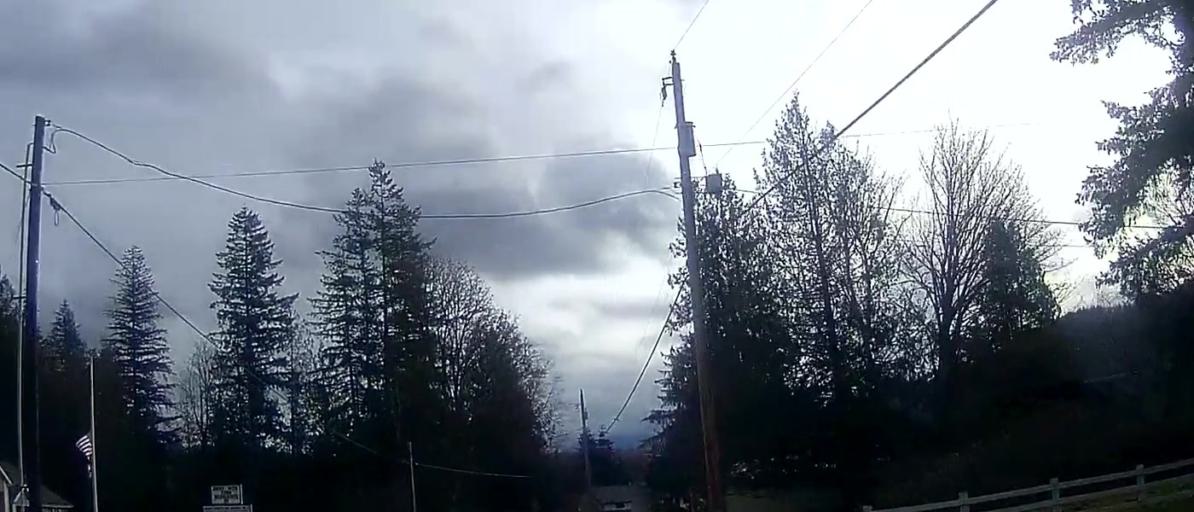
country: US
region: Washington
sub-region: Skagit County
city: Sedro-Woolley
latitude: 48.5623
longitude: -122.2921
